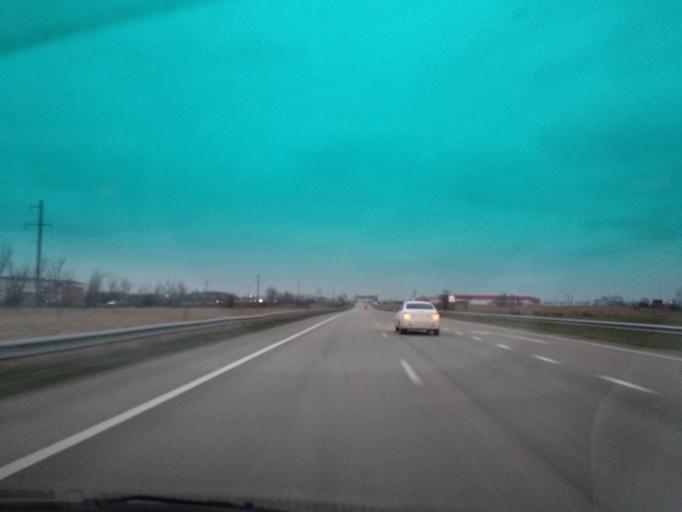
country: RU
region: Adygeya
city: Adygeysk
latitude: 44.8809
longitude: 39.1774
